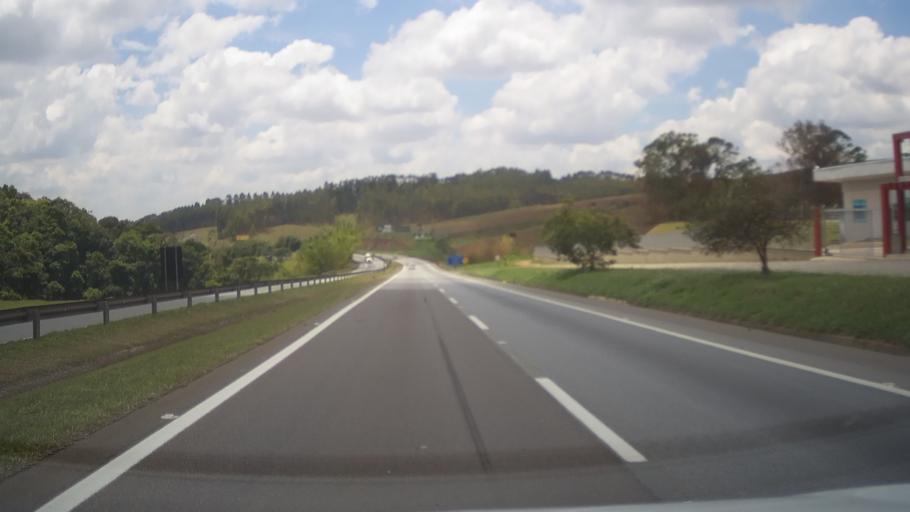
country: BR
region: Minas Gerais
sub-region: Tres Coracoes
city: Tres Coracoes
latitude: -21.6951
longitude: -45.3573
